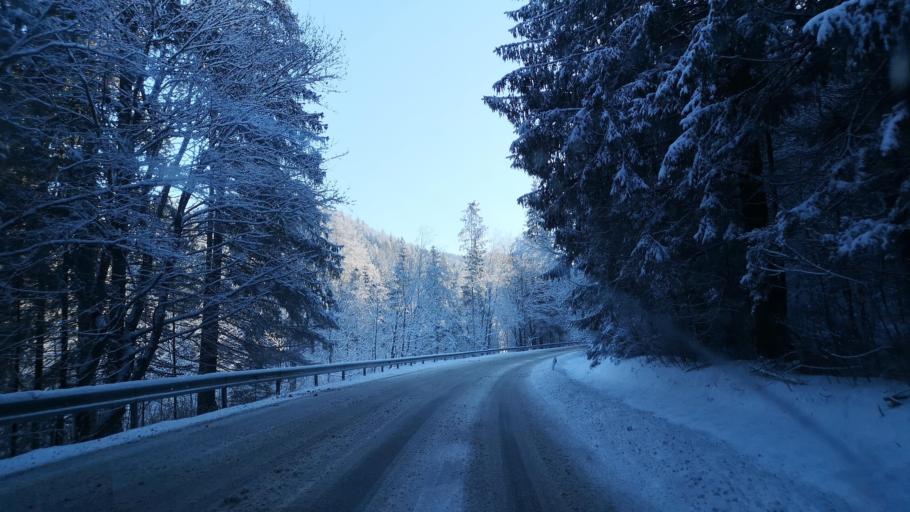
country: SK
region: Banskobystricky
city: Revuca
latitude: 48.8291
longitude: 20.1192
